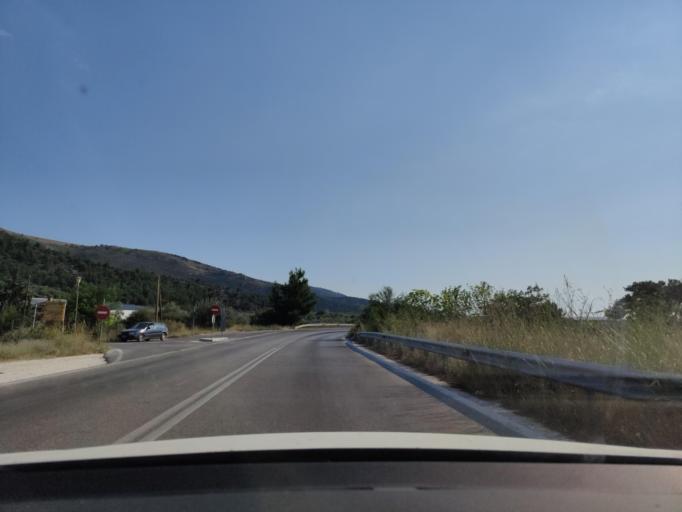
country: GR
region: East Macedonia and Thrace
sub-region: Nomos Kavalas
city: Prinos
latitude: 40.7596
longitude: 24.5907
